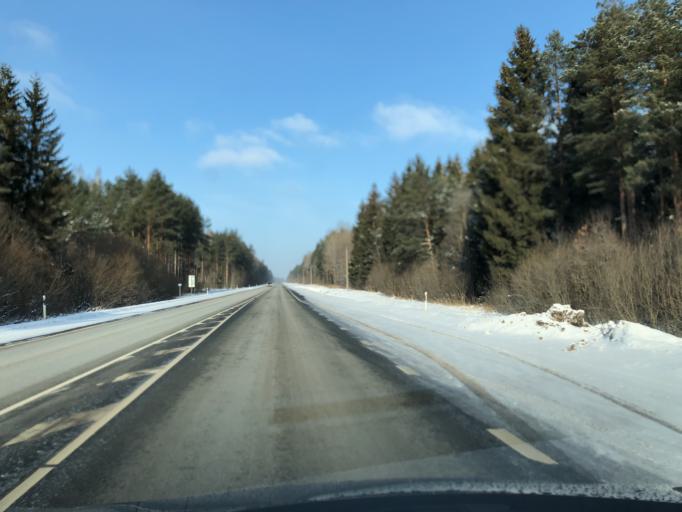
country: EE
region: Tartu
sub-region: Tartu linn
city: Tartu
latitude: 58.3883
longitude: 26.6680
